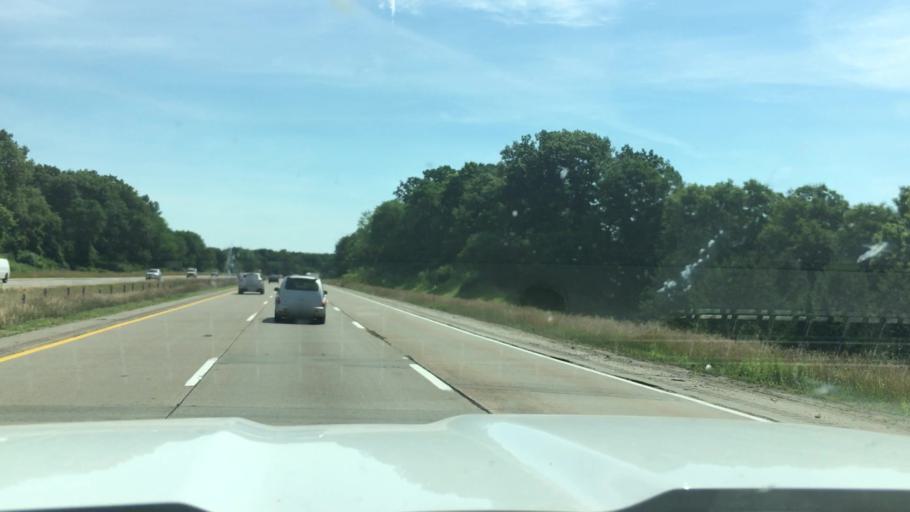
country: US
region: Michigan
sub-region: Ionia County
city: Portland
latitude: 42.8603
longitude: -84.9096
